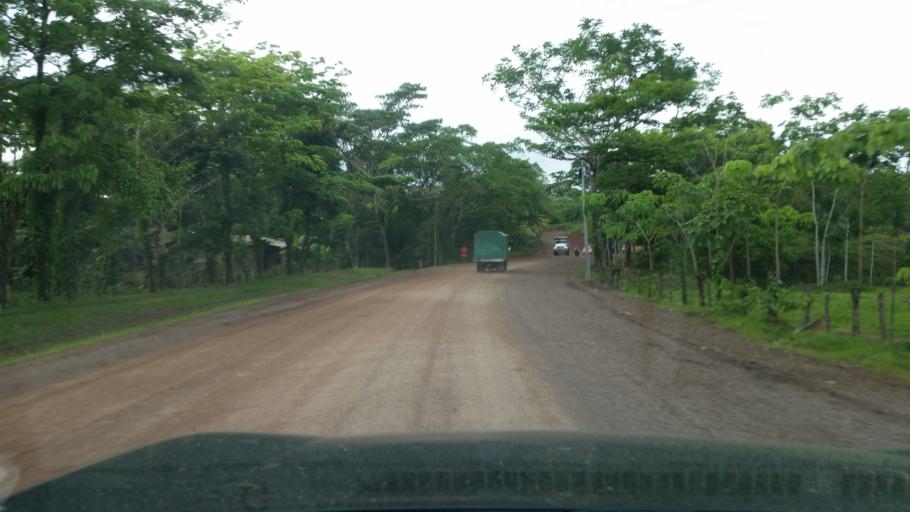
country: NI
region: Matagalpa
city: Rio Blanco
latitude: 13.2065
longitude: -84.9499
